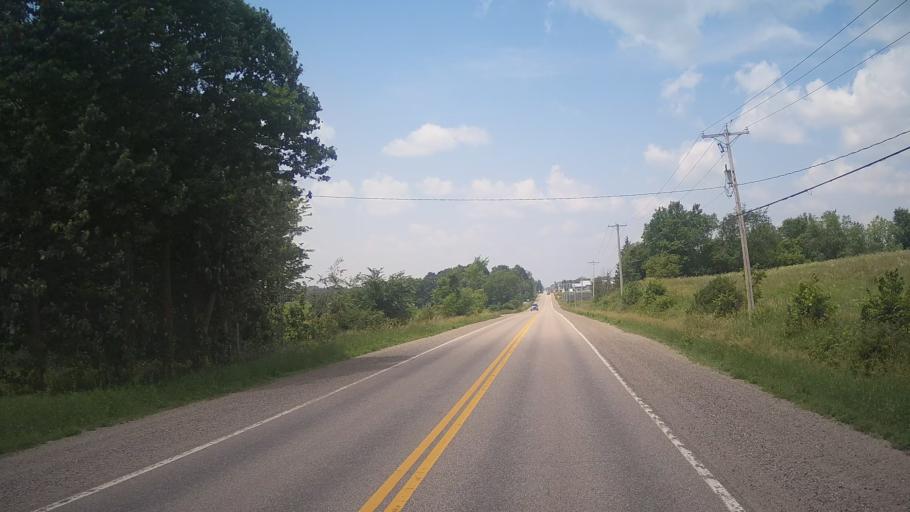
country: CA
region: Quebec
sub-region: Outaouais
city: Shawville
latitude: 45.5937
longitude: -76.4776
